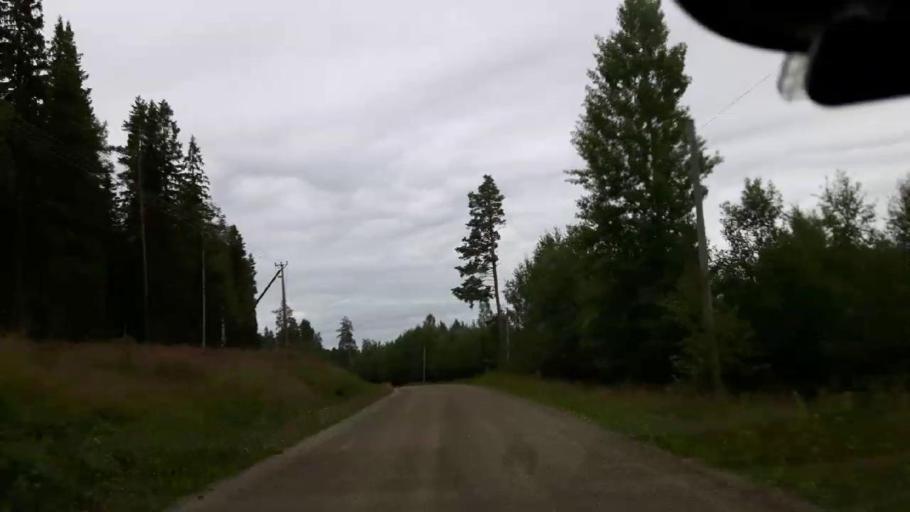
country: SE
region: Jaemtland
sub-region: Braecke Kommun
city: Braecke
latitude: 63.0162
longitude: 15.3766
